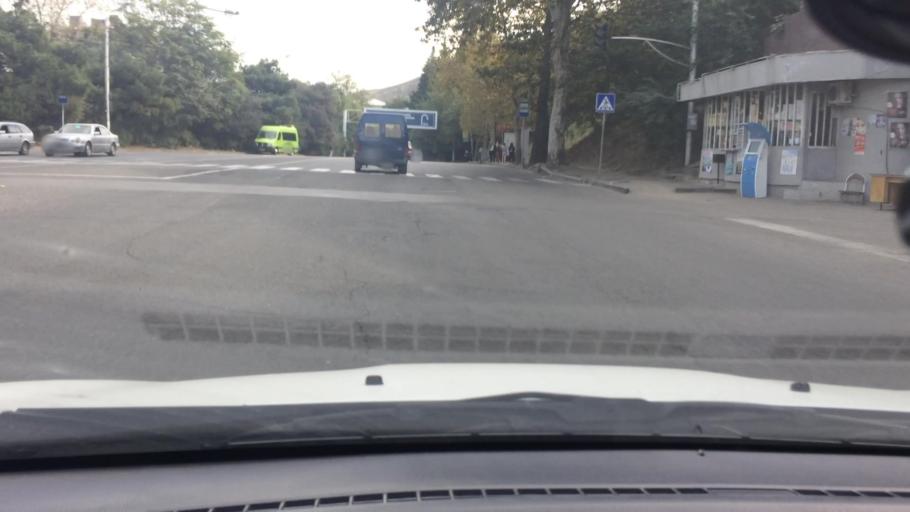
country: GE
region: T'bilisi
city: Tbilisi
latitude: 41.6725
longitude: 44.8343
